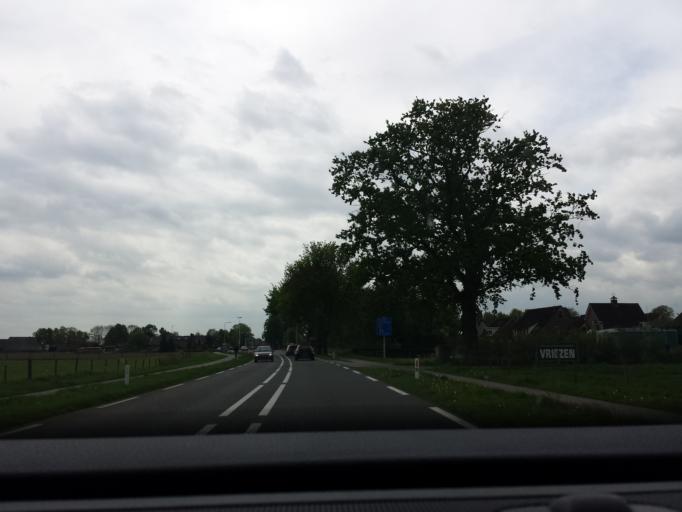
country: NL
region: Gelderland
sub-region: Gemeente Doetinchem
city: Doetinchem
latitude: 51.9259
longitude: 6.2697
